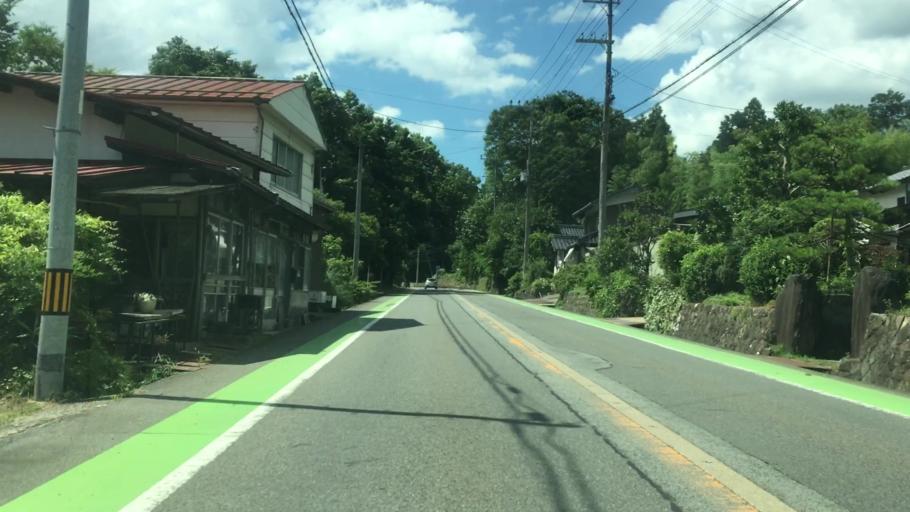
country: JP
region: Hyogo
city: Toyooka
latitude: 35.4753
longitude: 134.7125
